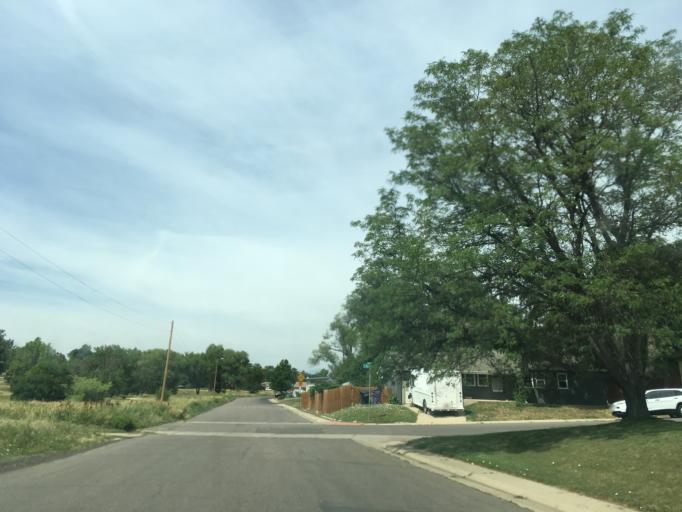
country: US
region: Colorado
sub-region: Arapahoe County
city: Sheridan
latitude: 39.6855
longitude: -105.0376
